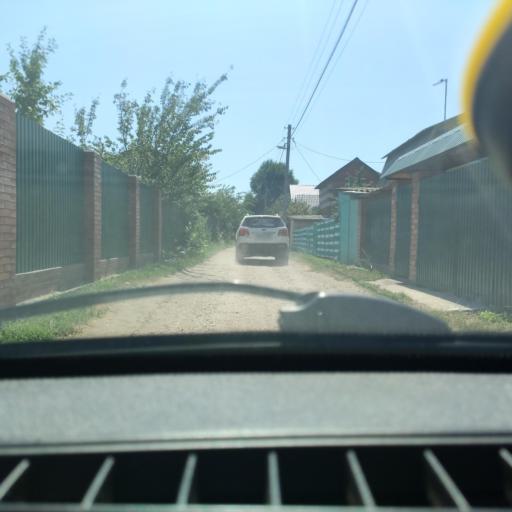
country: RU
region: Samara
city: Tol'yatti
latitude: 53.5968
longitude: 49.3059
